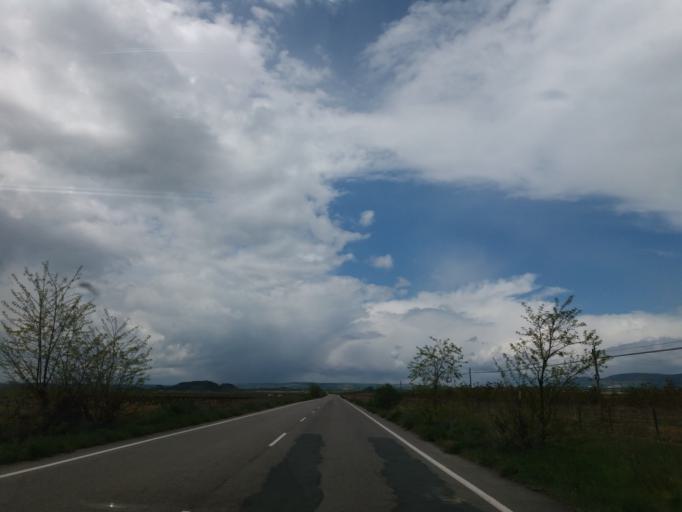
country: ES
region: La Rioja
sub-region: Provincia de La Rioja
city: Cihuri
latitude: 42.5738
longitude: -2.9351
